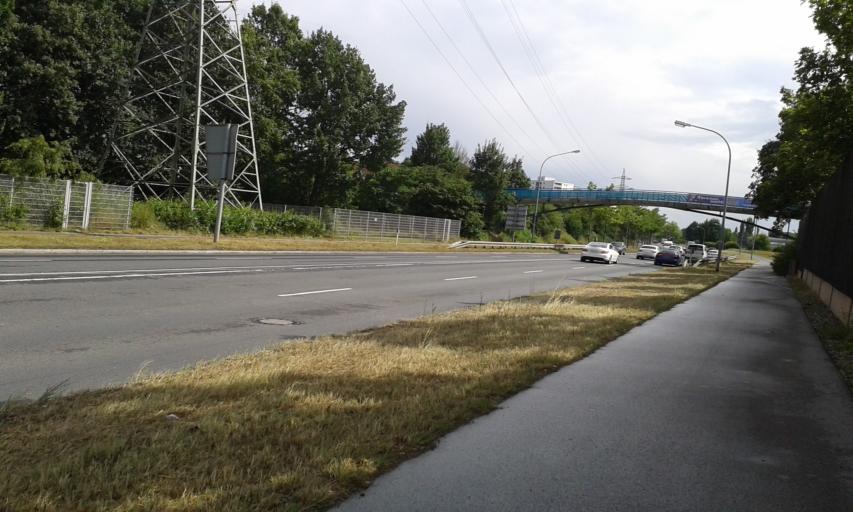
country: DE
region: Bavaria
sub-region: Upper Franconia
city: Bamberg
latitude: 49.8991
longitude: 10.9199
